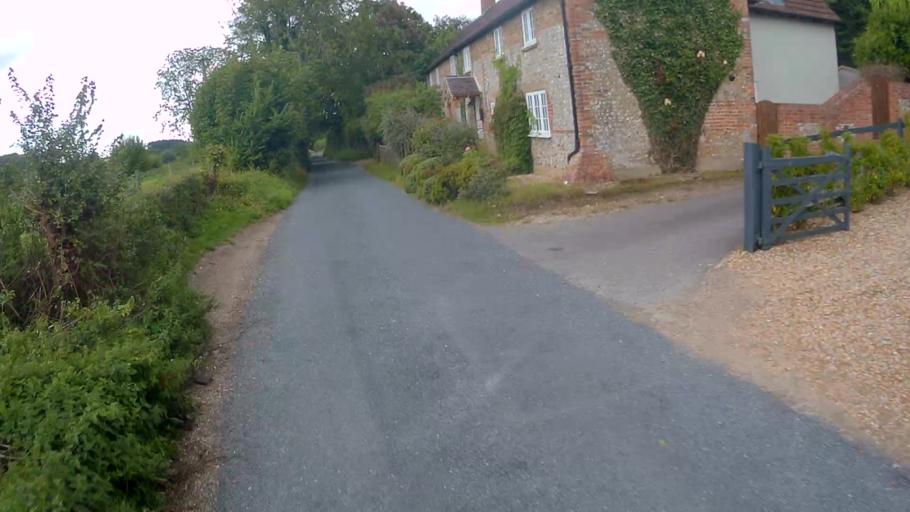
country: GB
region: England
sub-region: Hampshire
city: Basingstoke
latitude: 51.2073
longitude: -1.1657
